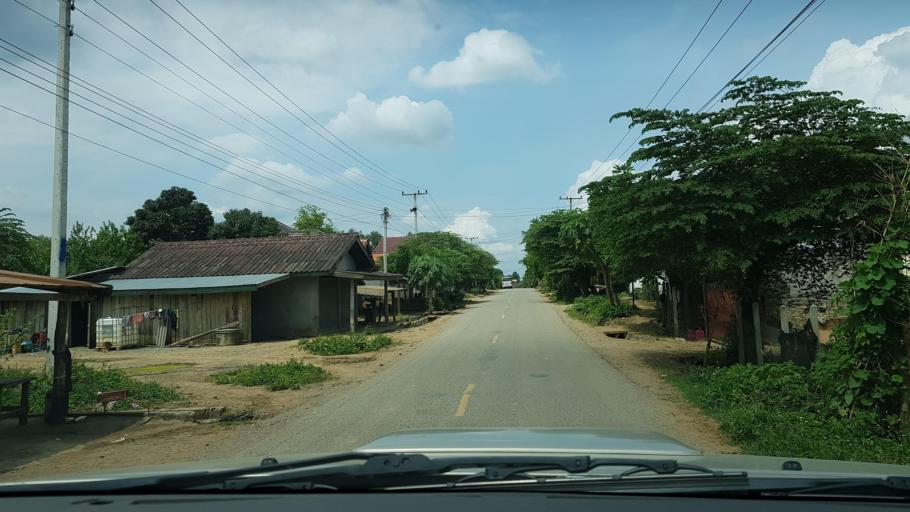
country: LA
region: Loungnamtha
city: Muang Nale
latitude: 20.0467
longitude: 101.3540
